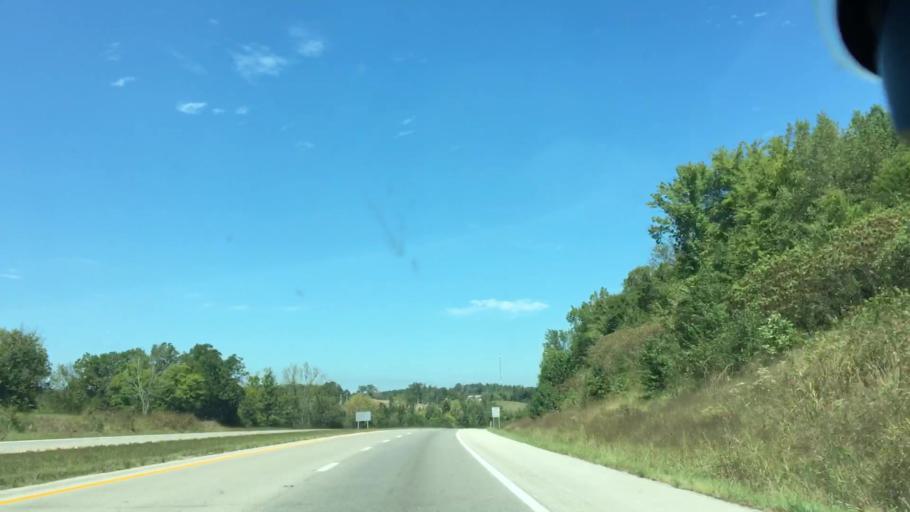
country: US
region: Kentucky
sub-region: Christian County
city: Hopkinsville
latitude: 36.9083
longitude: -87.4737
